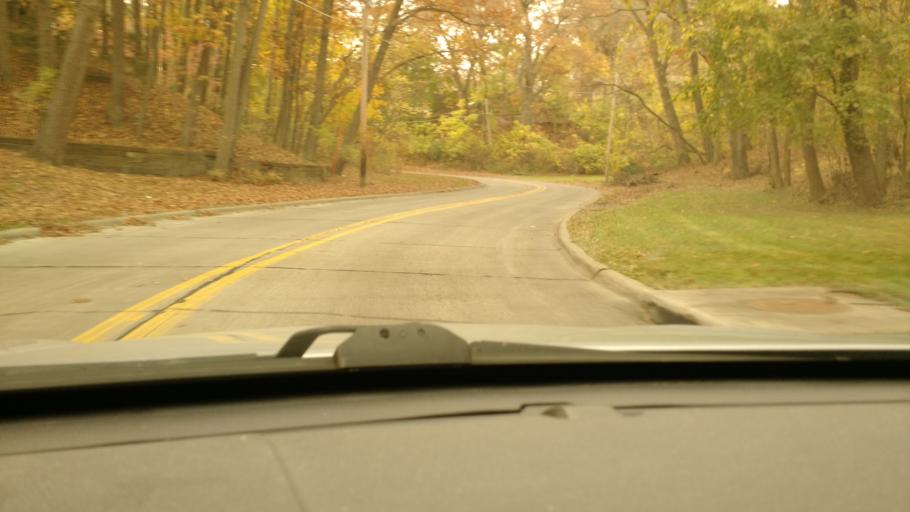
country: US
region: Illinois
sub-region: Rock Island County
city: Moline
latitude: 41.4871
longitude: -90.5246
